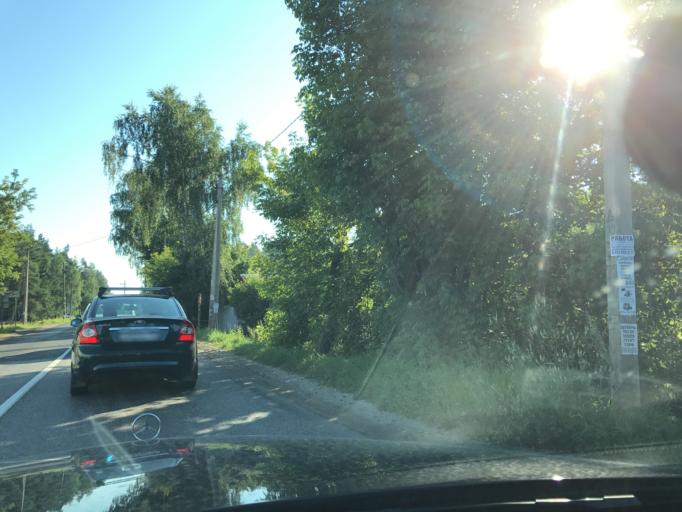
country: RU
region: Moskovskaya
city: Sverdlovskiy
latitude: 55.8594
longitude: 38.1383
